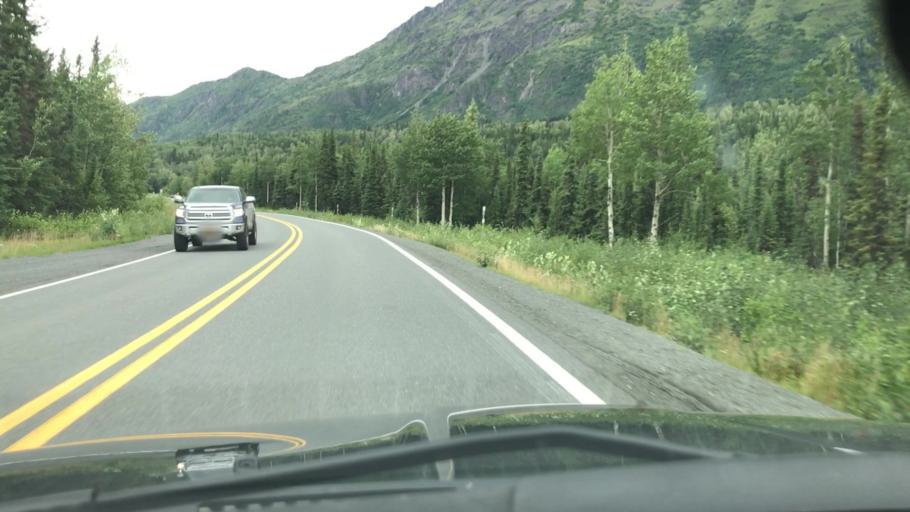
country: US
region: Alaska
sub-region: Kenai Peninsula Borough
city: Seward
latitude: 60.4862
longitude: -149.9645
